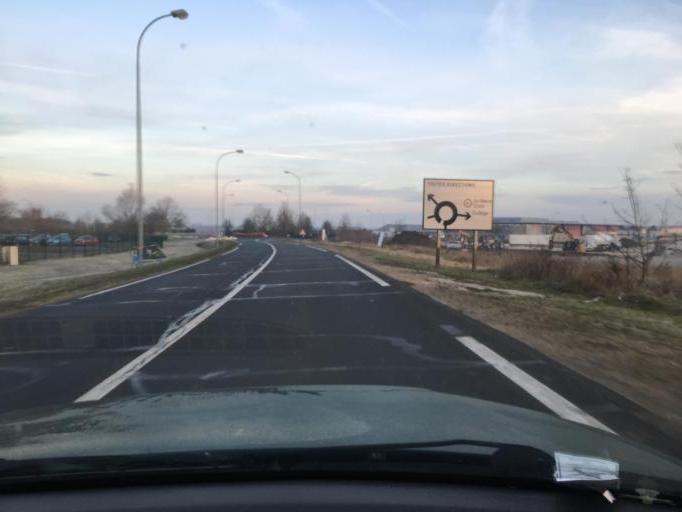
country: FR
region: Centre
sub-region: Departement du Loiret
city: Meung-sur-Loire
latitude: 47.8297
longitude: 1.6789
